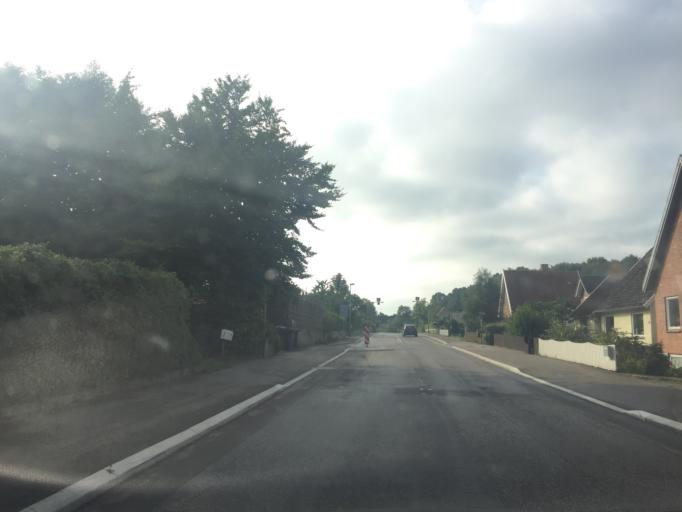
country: DK
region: Capital Region
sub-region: Halsnaes Kommune
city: Frederiksvaerk
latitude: 55.9542
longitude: 12.0247
